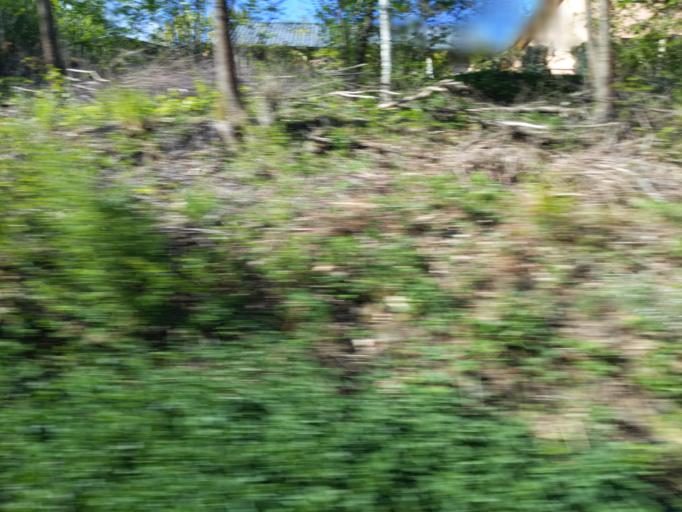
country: DE
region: Saxony
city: Radeberg
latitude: 51.1219
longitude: 13.8715
